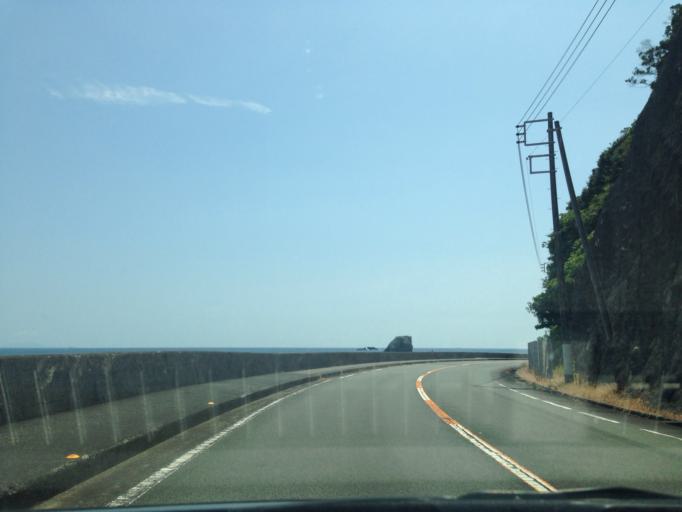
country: JP
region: Shizuoka
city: Shimoda
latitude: 34.6189
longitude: 138.8648
